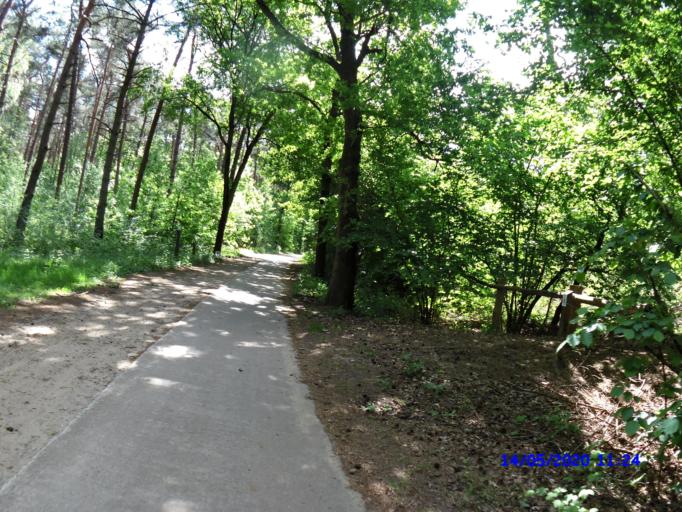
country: BE
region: Flanders
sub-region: Provincie Antwerpen
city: Kasterlee
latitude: 51.2162
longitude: 4.8987
